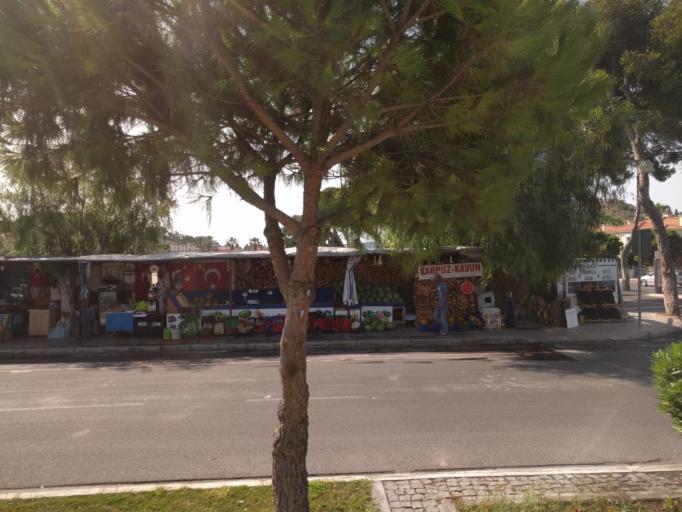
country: TR
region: Izmir
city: Alacati
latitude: 38.2867
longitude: 26.3699
